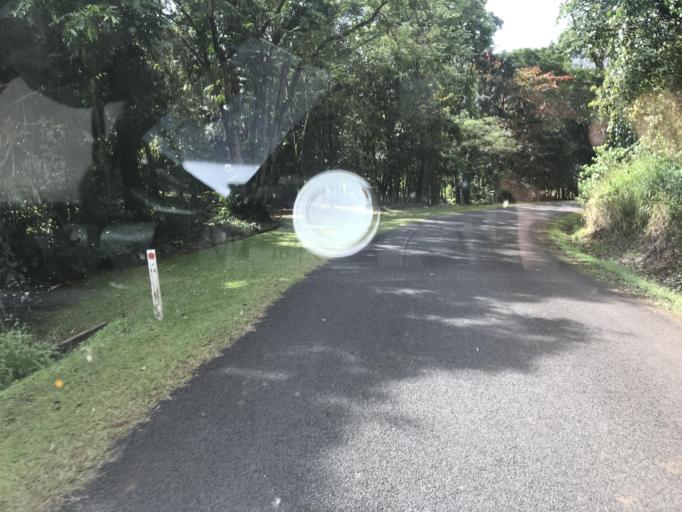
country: AU
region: Queensland
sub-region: Cassowary Coast
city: Innisfail
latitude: -17.5499
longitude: 145.8681
